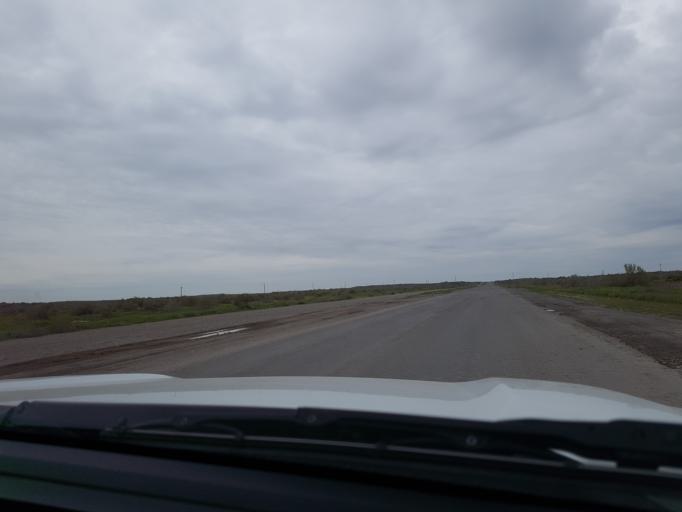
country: TM
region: Mary
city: Bayramaly
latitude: 37.9226
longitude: 62.6241
